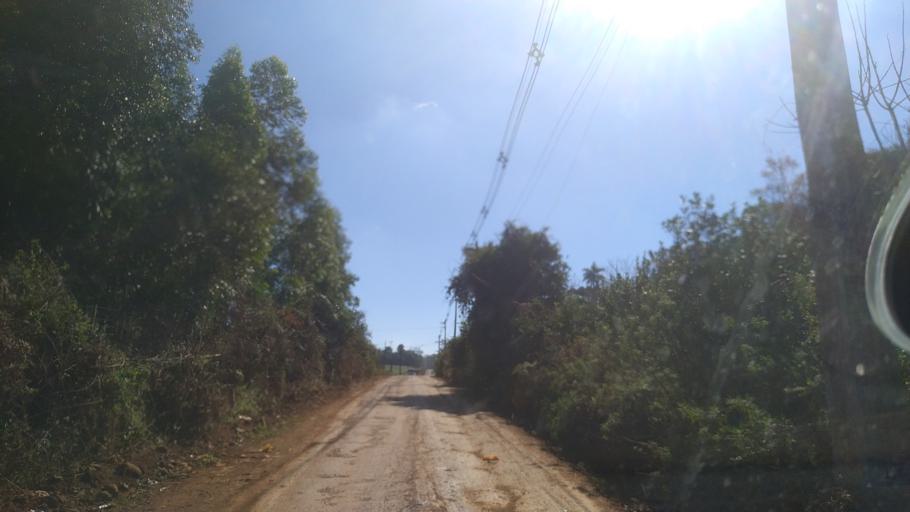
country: BR
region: Santa Catarina
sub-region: Chapeco
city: Chapeco
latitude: -27.0922
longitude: -52.6937
